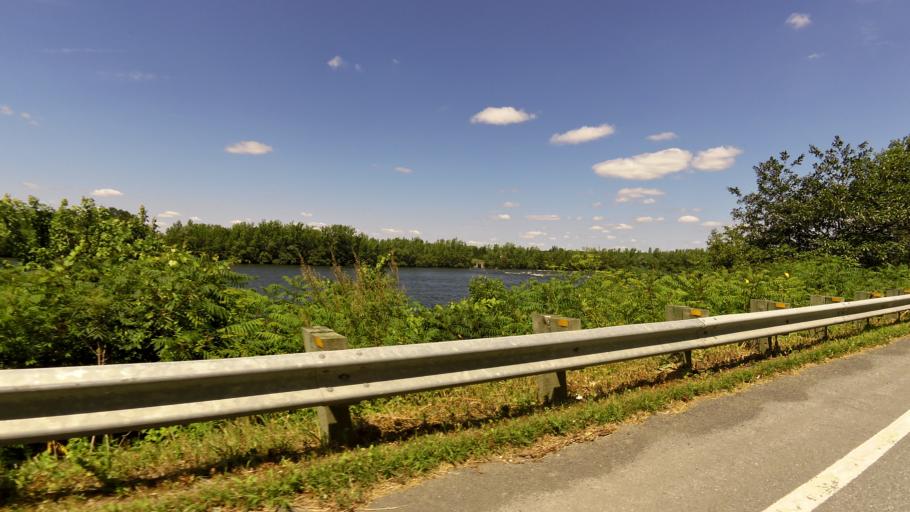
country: CA
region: Quebec
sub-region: Monteregie
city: Richelieu
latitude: 45.4017
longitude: -73.2542
